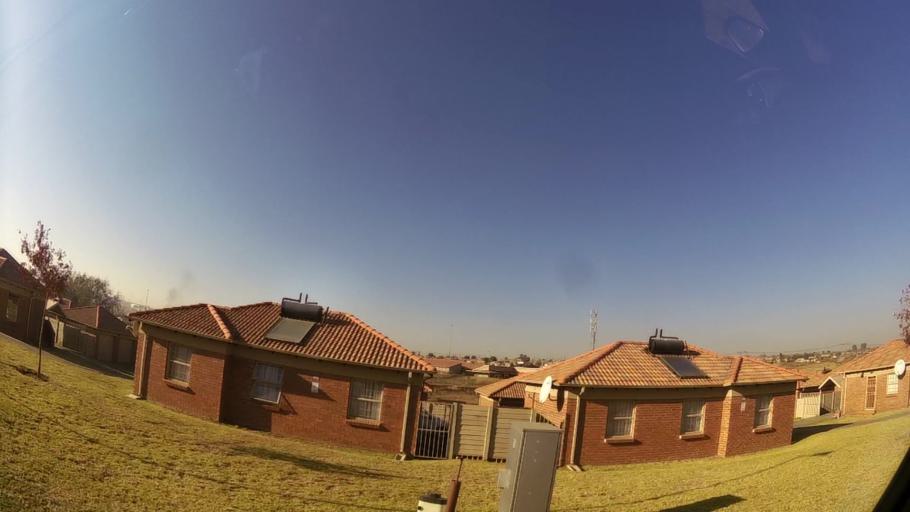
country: ZA
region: Gauteng
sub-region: City of Johannesburg Metropolitan Municipality
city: Midrand
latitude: -25.9103
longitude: 28.1099
